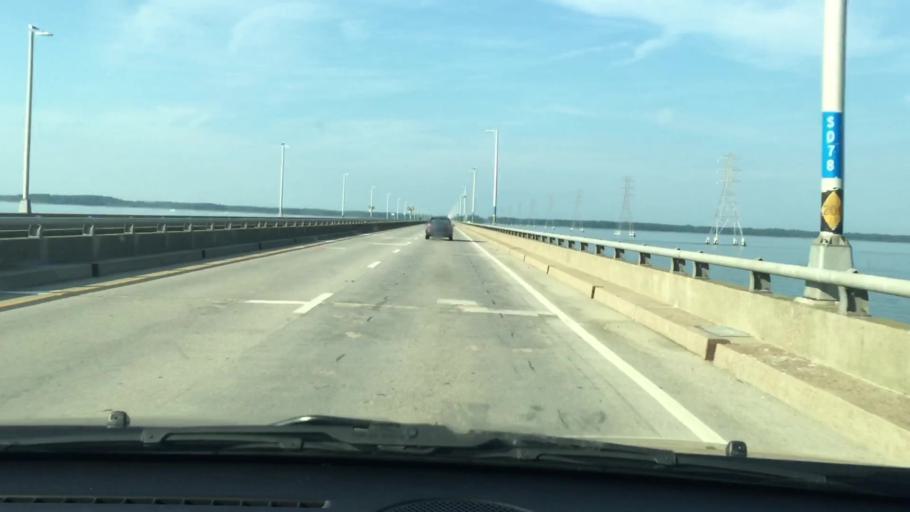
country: US
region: Virginia
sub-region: City of Newport News
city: Newport News
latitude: 36.9906
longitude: -76.4839
